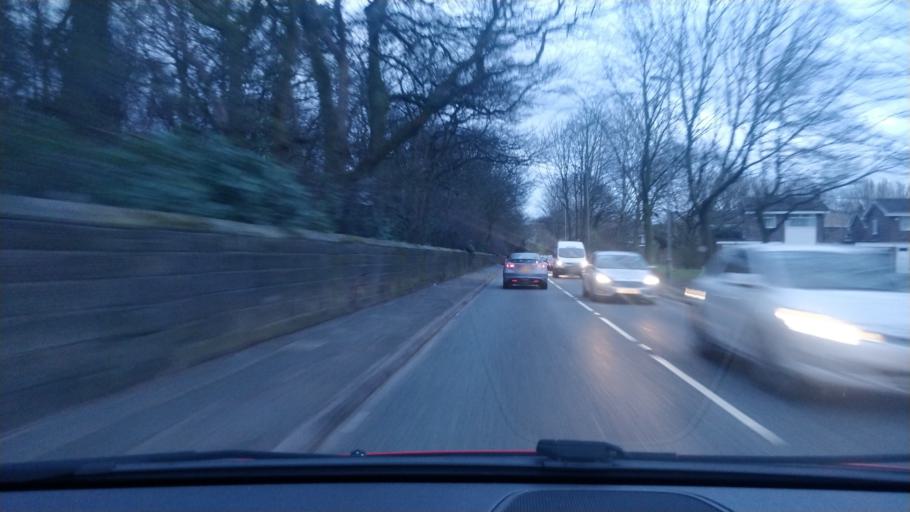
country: GB
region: England
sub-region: Knowsley
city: Kirkby
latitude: 53.4455
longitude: -2.8986
